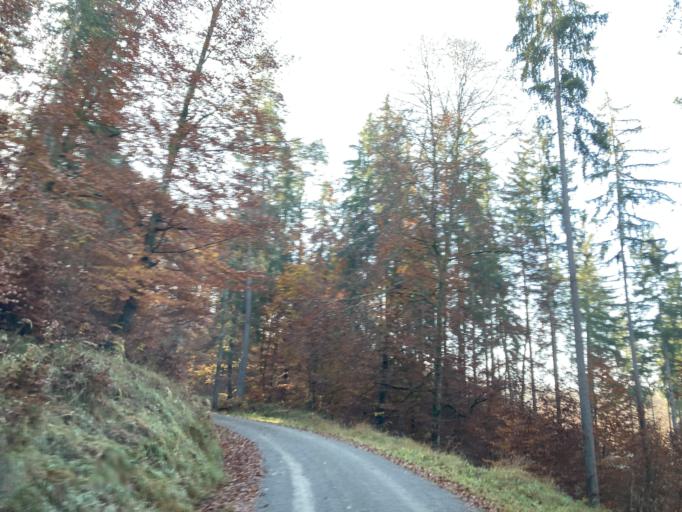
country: DE
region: Baden-Wuerttemberg
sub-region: Regierungsbezirk Stuttgart
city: Hildrizhausen
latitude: 48.5810
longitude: 8.9813
